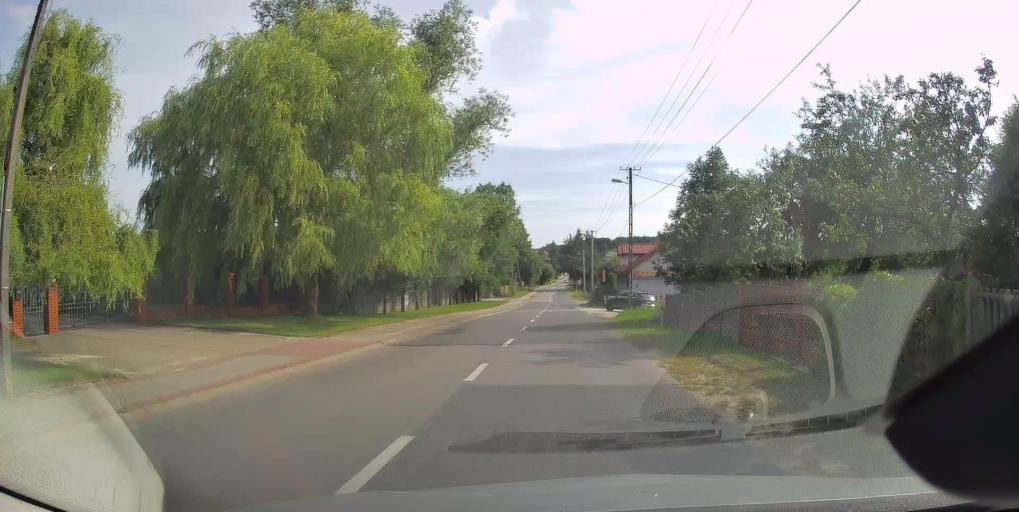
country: PL
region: Lodz Voivodeship
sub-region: Powiat tomaszowski
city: Tomaszow Mazowiecki
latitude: 51.4872
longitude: 19.9887
